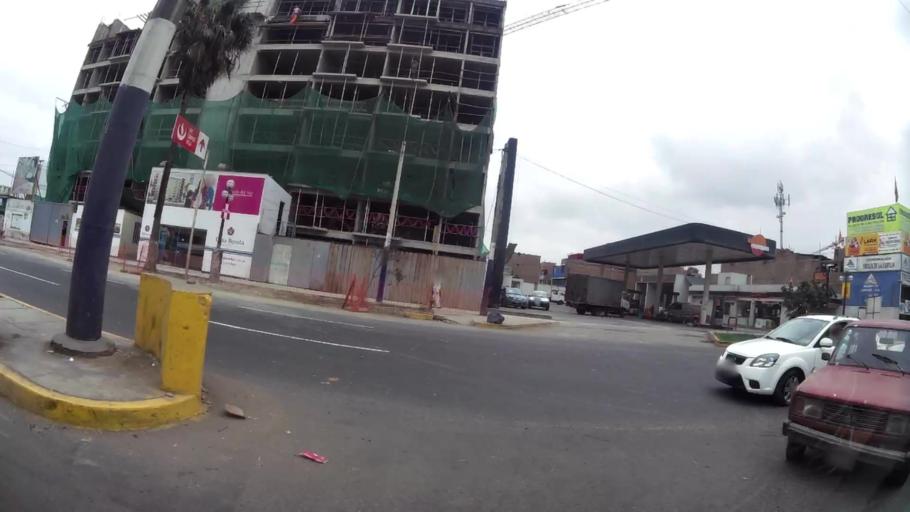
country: PE
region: Lima
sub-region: Lima
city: Surco
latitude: -12.1802
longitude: -76.9981
